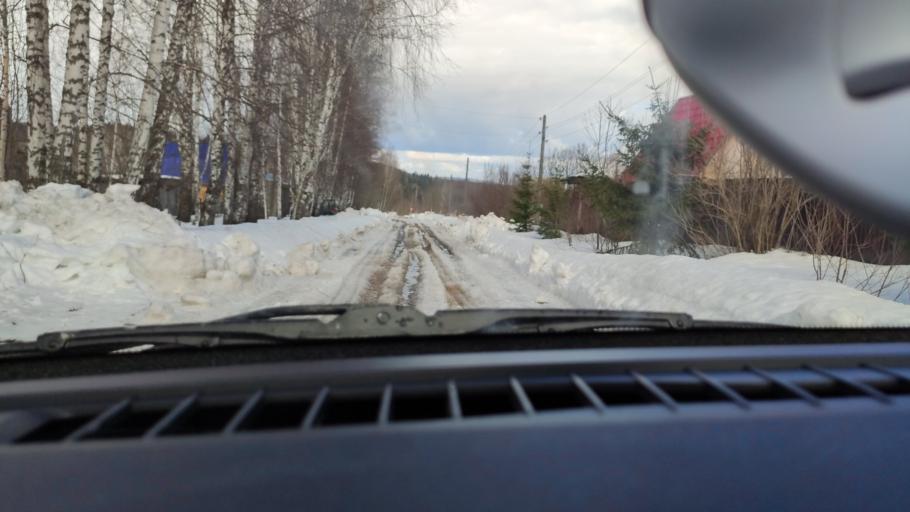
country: RU
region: Perm
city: Nytva
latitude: 57.9249
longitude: 55.4350
